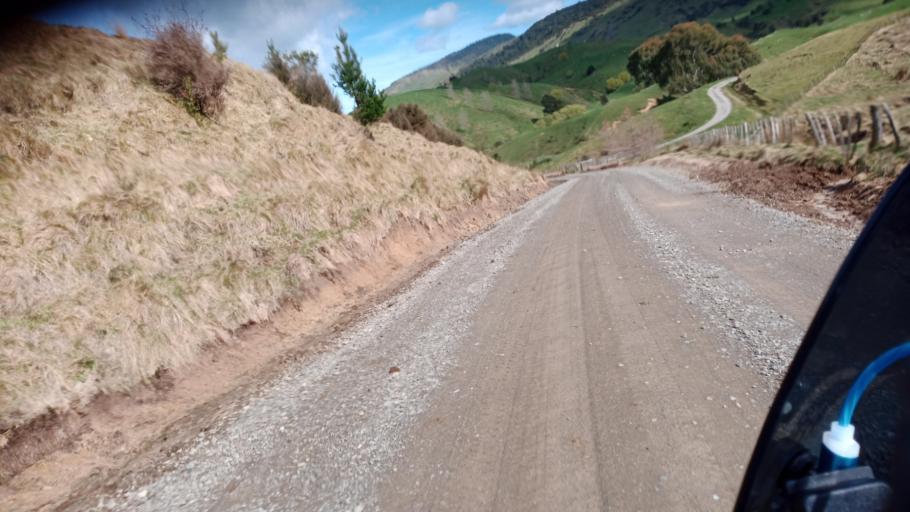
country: NZ
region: Hawke's Bay
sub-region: Wairoa District
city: Wairoa
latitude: -38.7386
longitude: 177.2945
